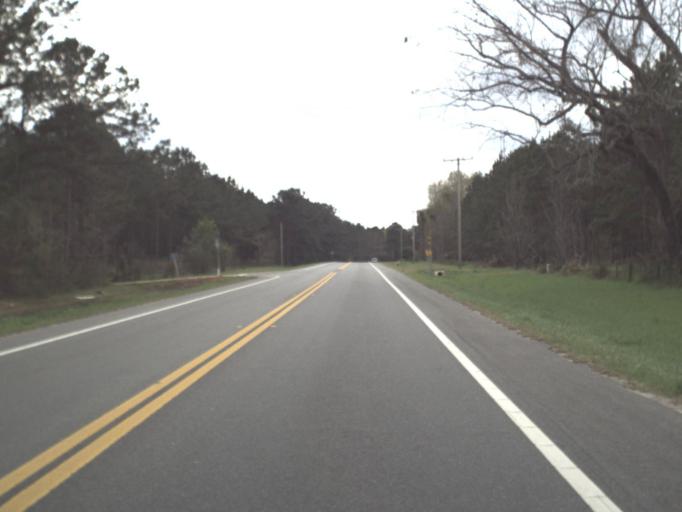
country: US
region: Florida
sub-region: Gadsden County
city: Quincy
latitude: 30.5307
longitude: -84.5990
